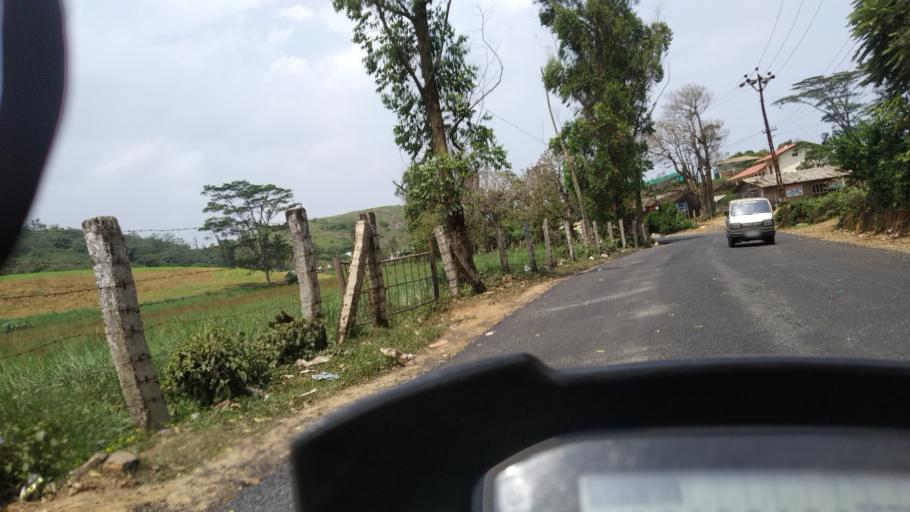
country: IN
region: Kerala
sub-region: Kottayam
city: Erattupetta
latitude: 9.6522
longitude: 76.9274
